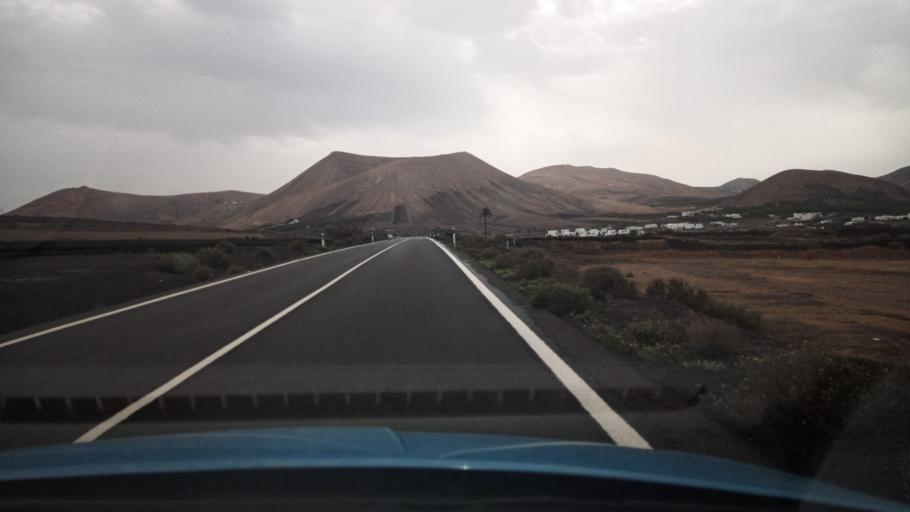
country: ES
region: Canary Islands
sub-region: Provincia de Las Palmas
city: Yaiza
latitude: 28.9537
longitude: -13.7370
